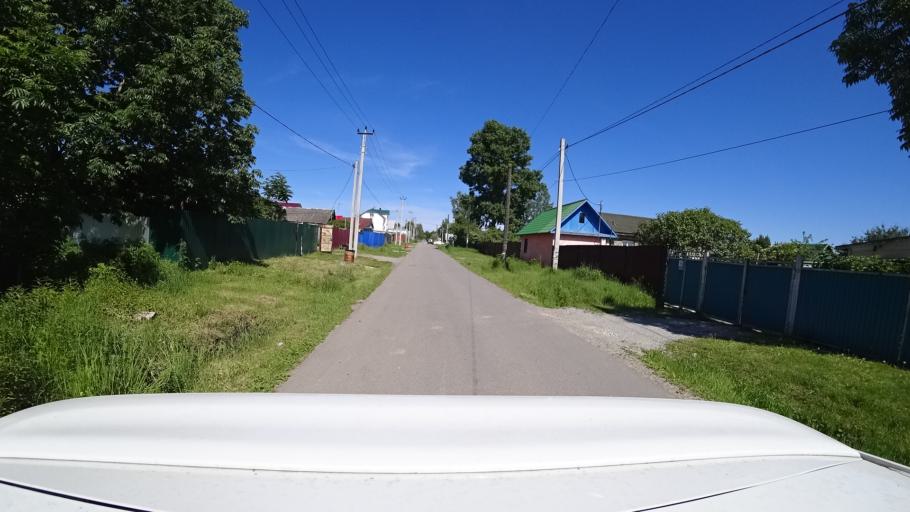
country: RU
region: Khabarovsk Krai
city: Topolevo
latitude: 48.5537
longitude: 135.1948
